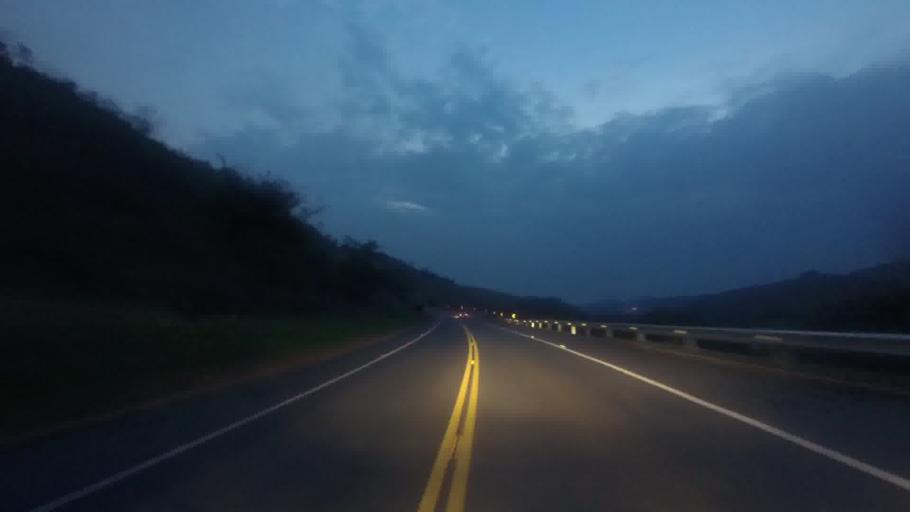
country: BR
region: Rio de Janeiro
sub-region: Sapucaia
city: Sapucaia
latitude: -21.9472
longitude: -42.8378
